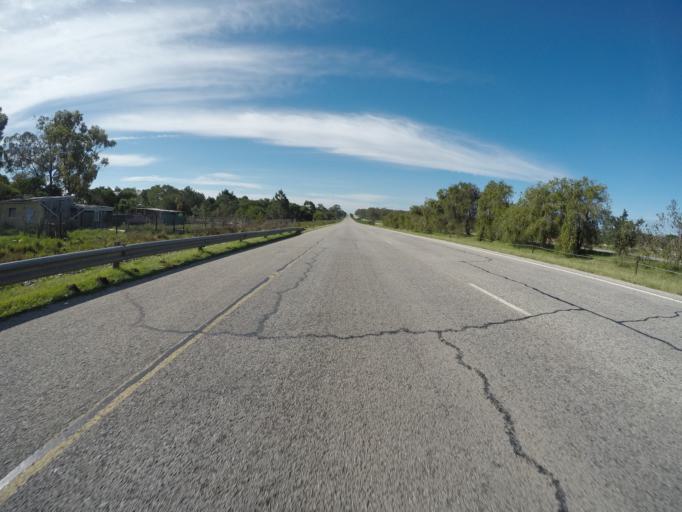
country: ZA
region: Eastern Cape
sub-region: Nelson Mandela Bay Metropolitan Municipality
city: Uitenhage
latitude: -33.9361
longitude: 25.3665
